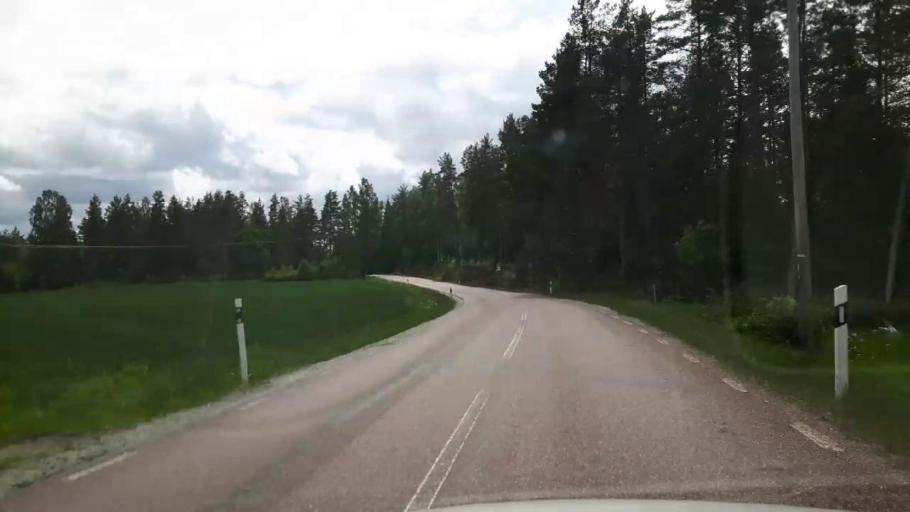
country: SE
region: Vaestmanland
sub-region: Fagersta Kommun
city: Fagersta
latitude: 59.9125
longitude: 15.8242
